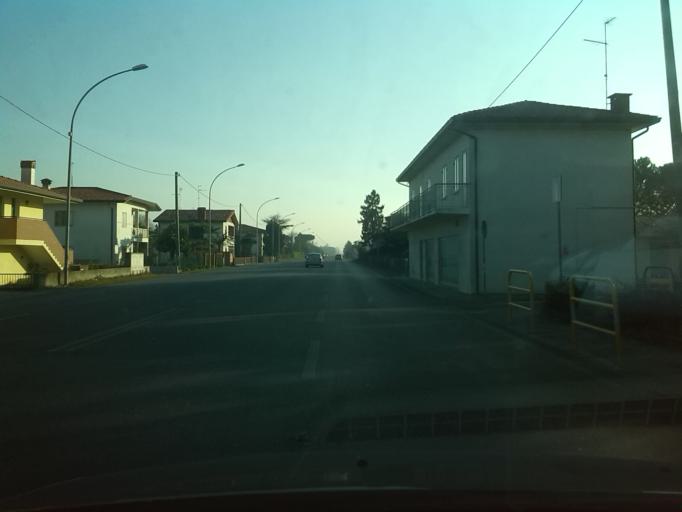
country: IT
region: Friuli Venezia Giulia
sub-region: Provincia di Udine
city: Pertegada
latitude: 45.7198
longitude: 13.0493
